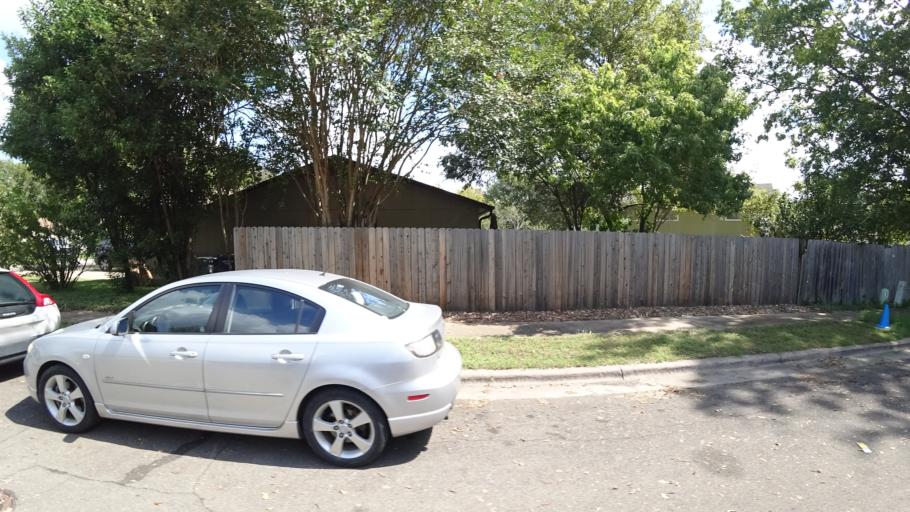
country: US
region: Texas
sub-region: Travis County
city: Onion Creek
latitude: 30.1846
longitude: -97.7910
